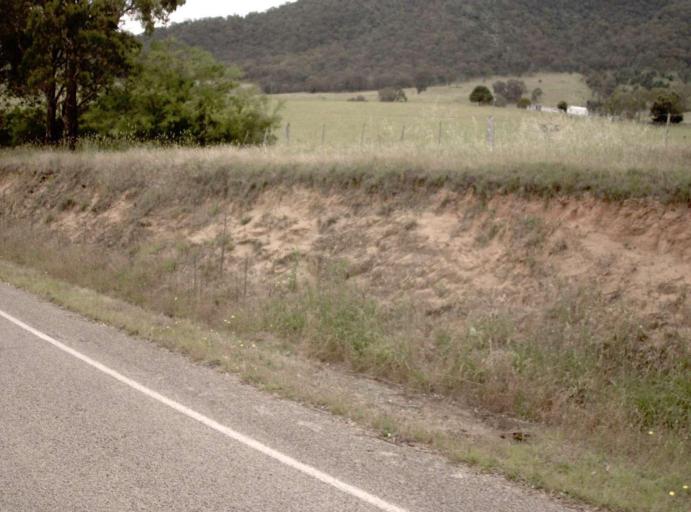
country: AU
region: Victoria
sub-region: East Gippsland
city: Bairnsdale
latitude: -37.5571
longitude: 147.1965
